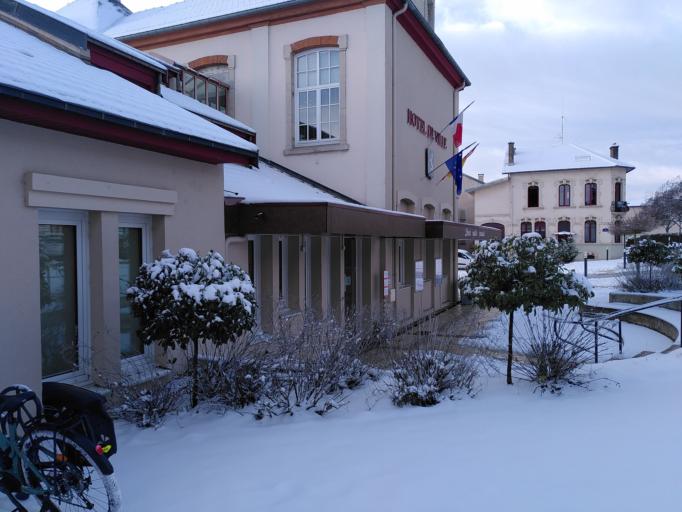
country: FR
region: Lorraine
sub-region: Departement de Meurthe-et-Moselle
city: Pompey
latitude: 48.7659
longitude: 6.1231
